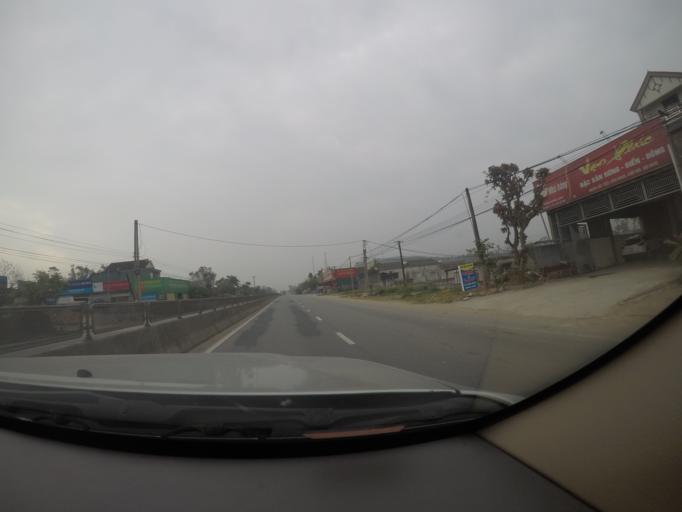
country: VN
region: Ha Tinh
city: Ky Anh
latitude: 18.1638
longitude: 106.2345
